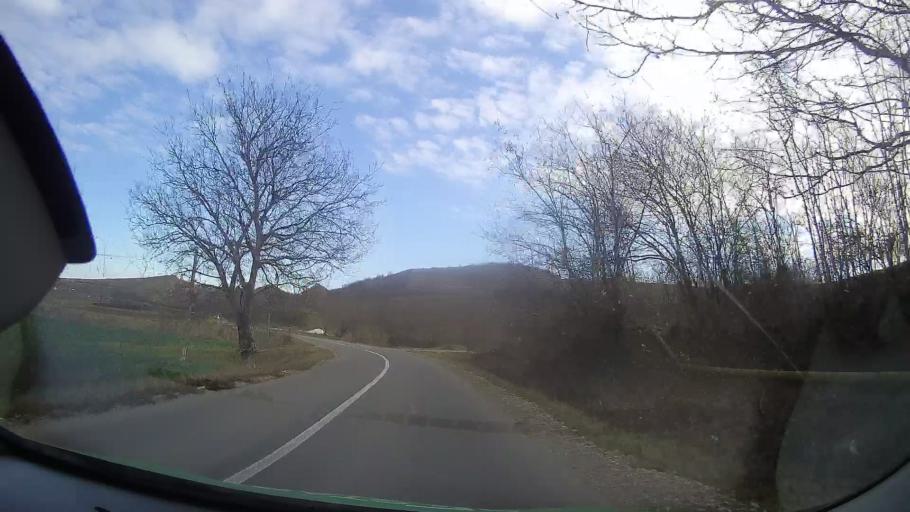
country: RO
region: Mures
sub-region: Comuna Iclanzel
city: Iclanzel
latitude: 46.5079
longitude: 24.2640
